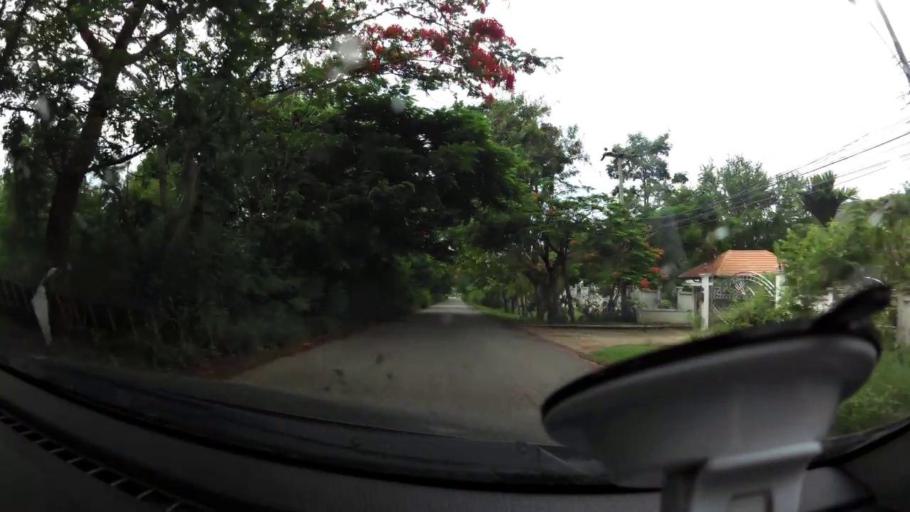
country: TH
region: Prachuap Khiri Khan
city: Pran Buri
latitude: 12.4415
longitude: 99.9699
